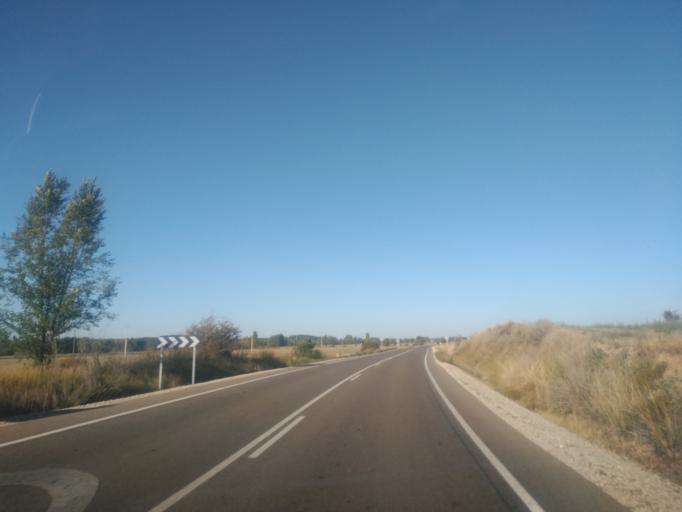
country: ES
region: Castille and Leon
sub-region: Provincia de Burgos
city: San Juan del Monte
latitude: 41.6911
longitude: -3.5245
